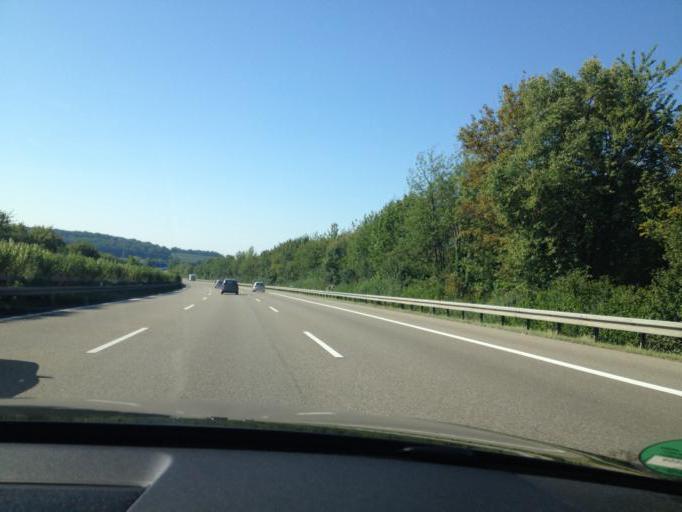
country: DE
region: Baden-Wuerttemberg
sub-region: Regierungsbezirk Stuttgart
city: Ilsfeld
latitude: 49.0210
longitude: 9.2481
